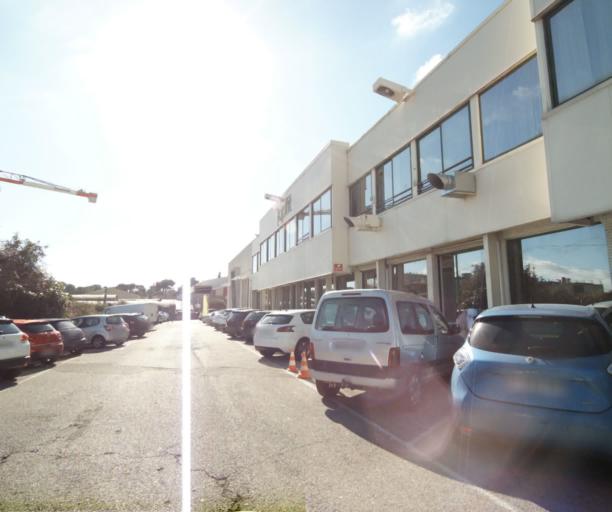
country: FR
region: Provence-Alpes-Cote d'Azur
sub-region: Departement des Alpes-Maritimes
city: Biot
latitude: 43.6005
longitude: 7.0833
